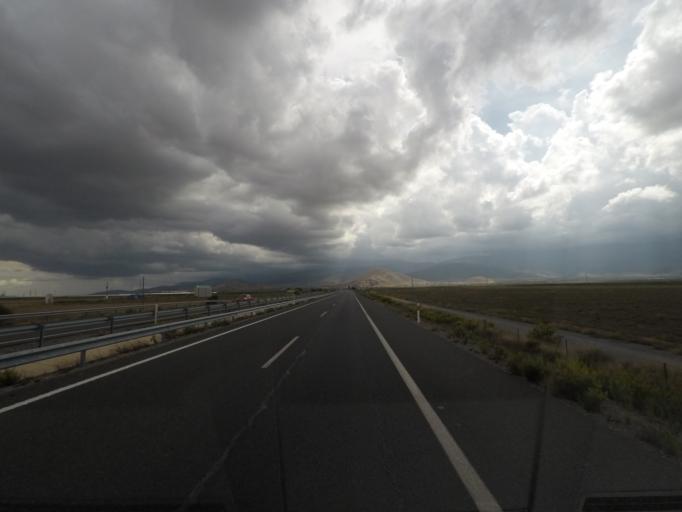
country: ES
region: Andalusia
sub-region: Provincia de Granada
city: Alquife
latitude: 37.2194
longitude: -3.0758
